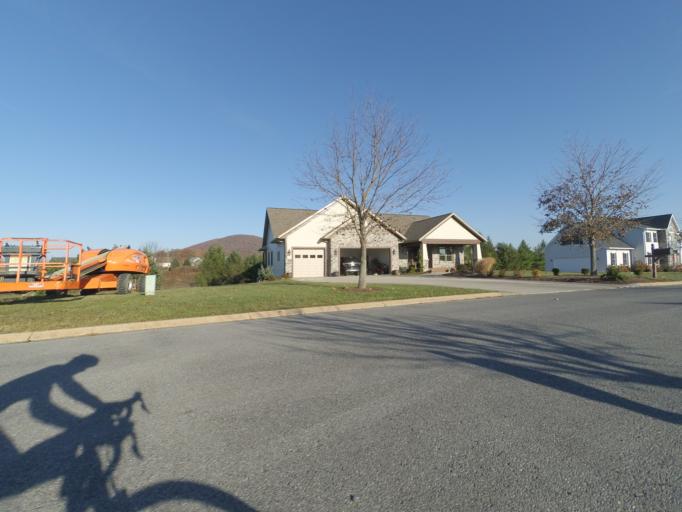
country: US
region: Pennsylvania
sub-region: Centre County
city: Lemont
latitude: 40.7961
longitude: -77.8230
